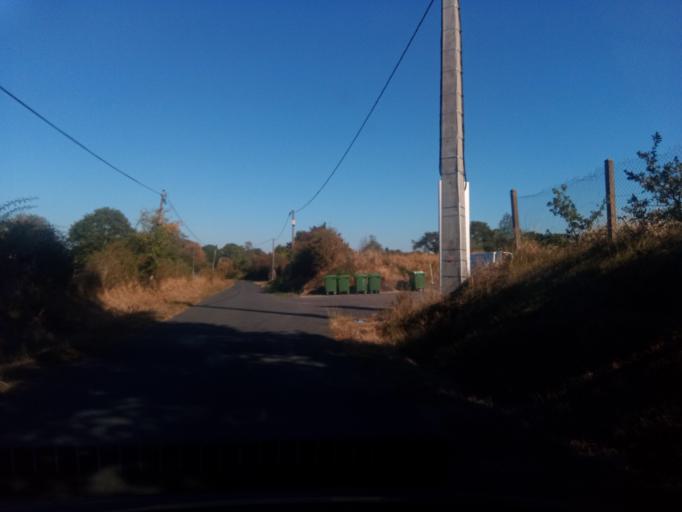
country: FR
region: Poitou-Charentes
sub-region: Departement de la Vienne
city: Montmorillon
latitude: 46.4263
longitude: 0.8532
